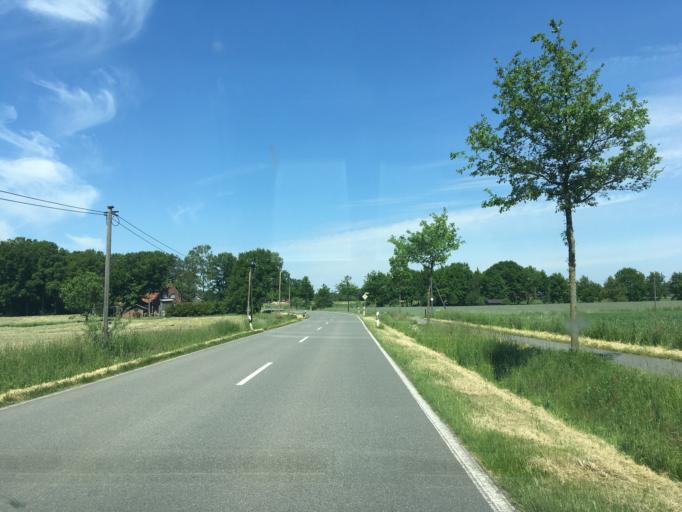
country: DE
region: North Rhine-Westphalia
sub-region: Regierungsbezirk Munster
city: Borken
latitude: 51.8693
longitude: 6.8329
